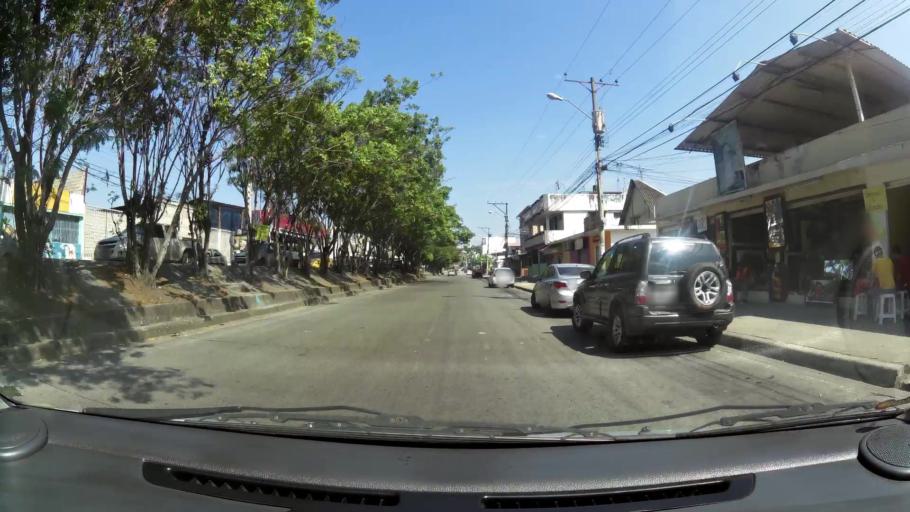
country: EC
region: Guayas
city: Eloy Alfaro
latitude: -2.1315
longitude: -79.9081
